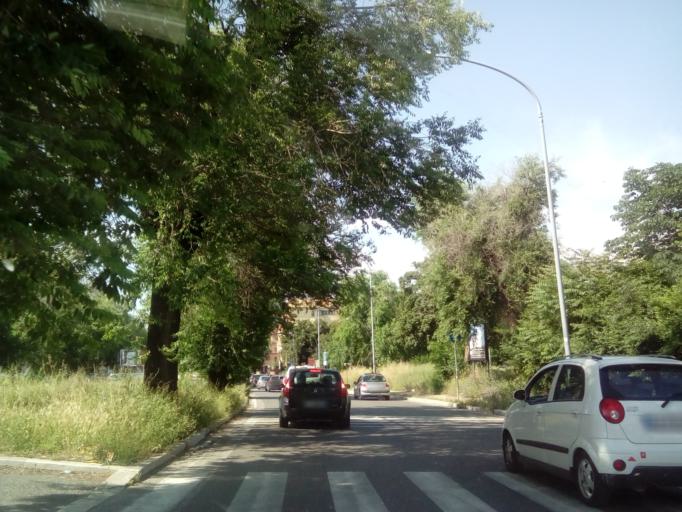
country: IT
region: Latium
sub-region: Citta metropolitana di Roma Capitale
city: Ciampino
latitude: 41.8549
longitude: 12.5713
